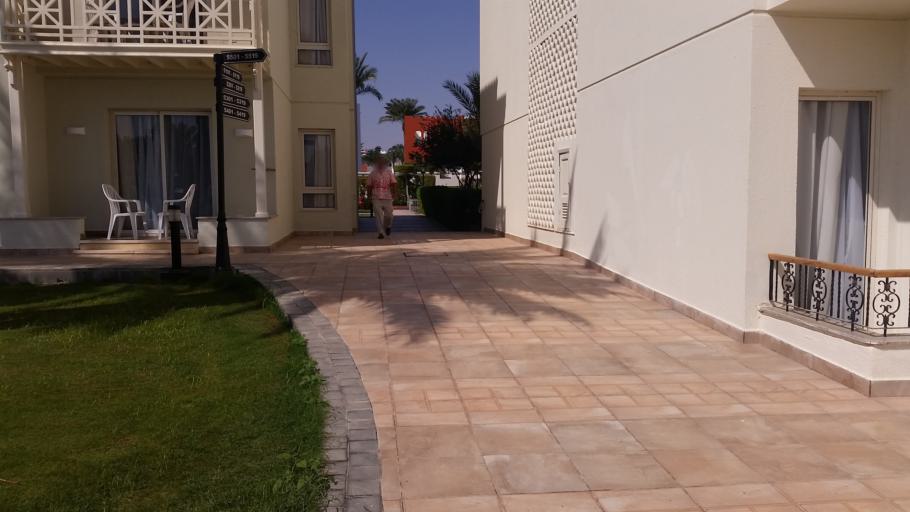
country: EG
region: Red Sea
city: Makadi Bay
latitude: 27.0988
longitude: 33.8321
